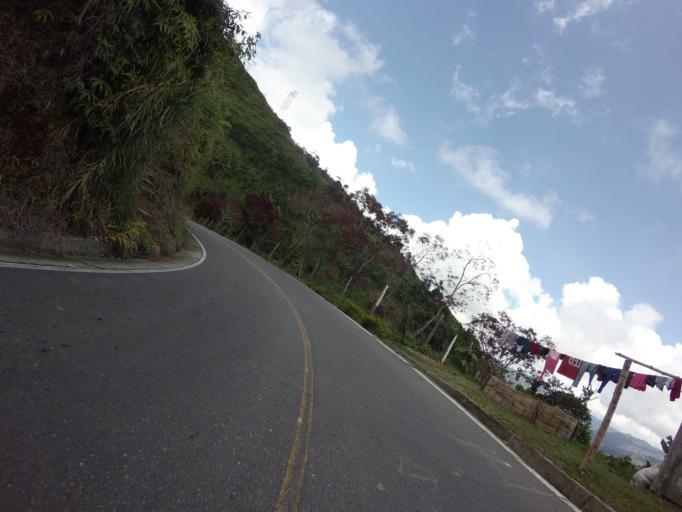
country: CO
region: Caldas
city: Marquetalia
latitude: 5.2768
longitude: -75.0997
